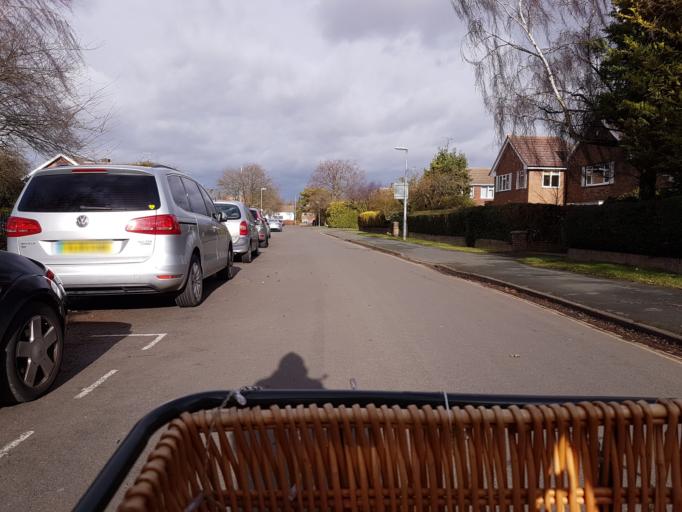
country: GB
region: England
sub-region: Cambridgeshire
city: Cambridge
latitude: 52.1777
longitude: 0.1513
